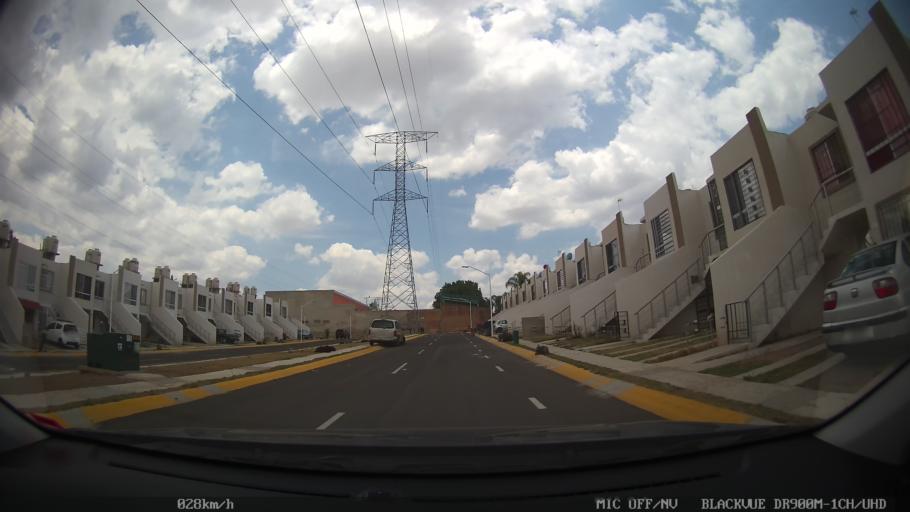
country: MX
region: Jalisco
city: Tonala
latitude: 20.6438
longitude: -103.2248
